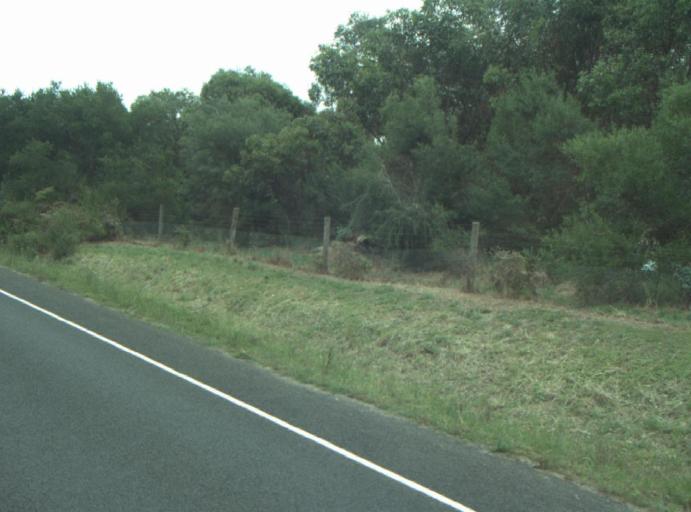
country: AU
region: Victoria
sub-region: Queenscliffe
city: Queenscliff
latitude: -38.2656
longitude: 144.5875
